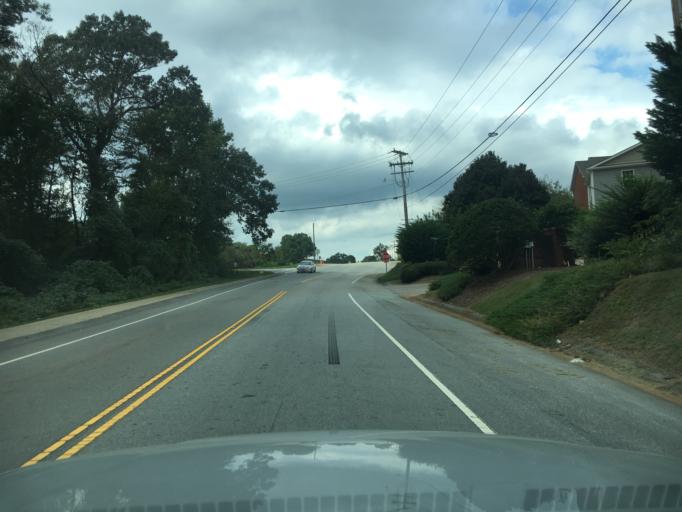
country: US
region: South Carolina
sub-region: Greenville County
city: Greer
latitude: 34.9550
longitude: -82.2323
